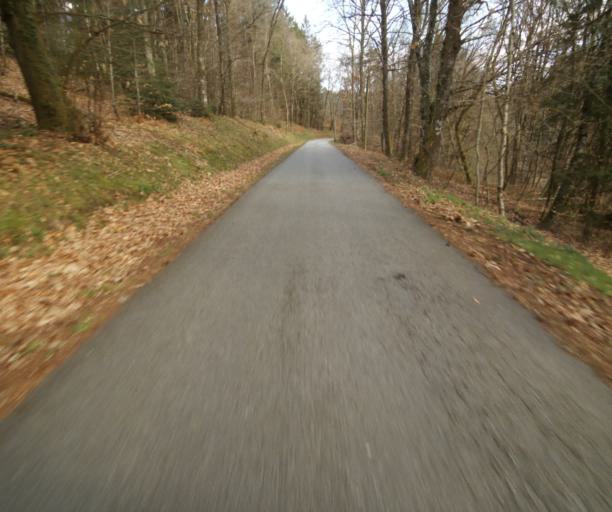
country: FR
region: Limousin
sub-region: Departement de la Correze
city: Correze
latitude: 45.3806
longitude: 1.8782
